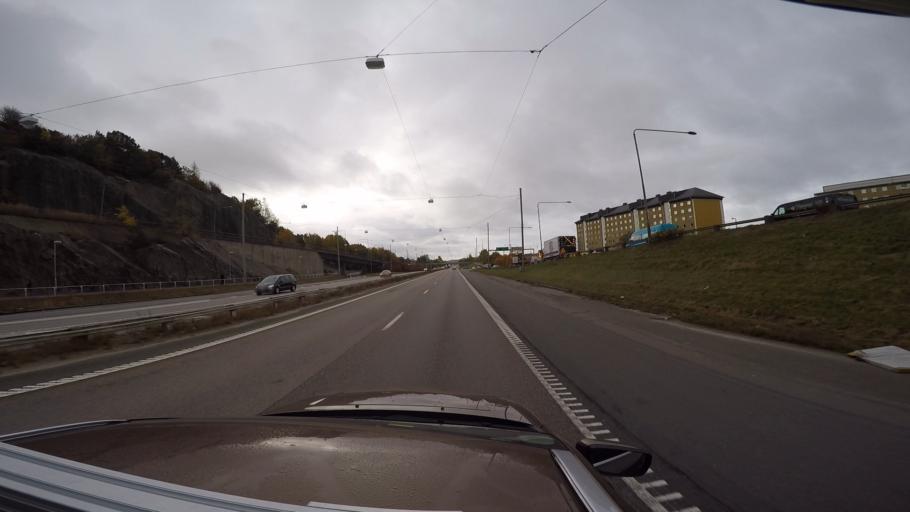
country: SE
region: Vaestra Goetaland
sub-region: Goteborg
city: Majorna
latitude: 57.6718
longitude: 11.9389
